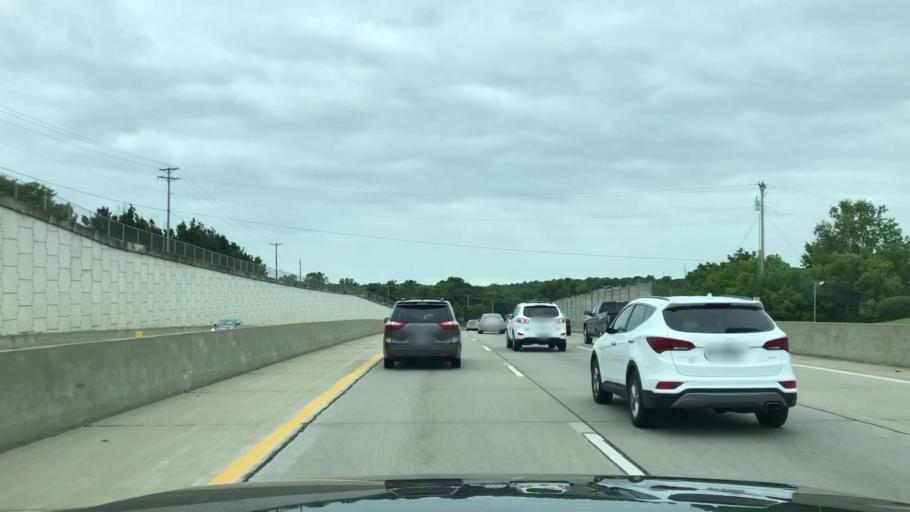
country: US
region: Missouri
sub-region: Saint Louis County
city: Manchester
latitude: 38.6019
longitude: -90.5097
